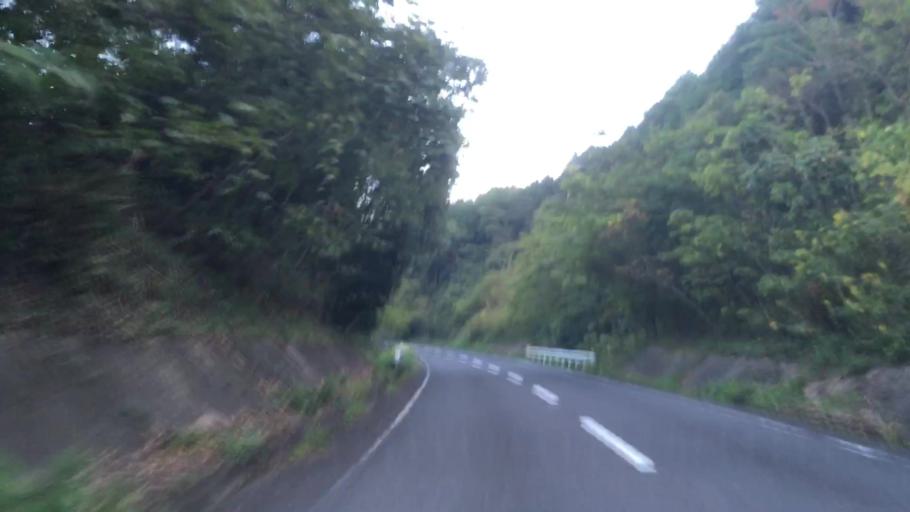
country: JP
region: Nagasaki
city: Sasebo
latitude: 33.0188
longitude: 129.7002
